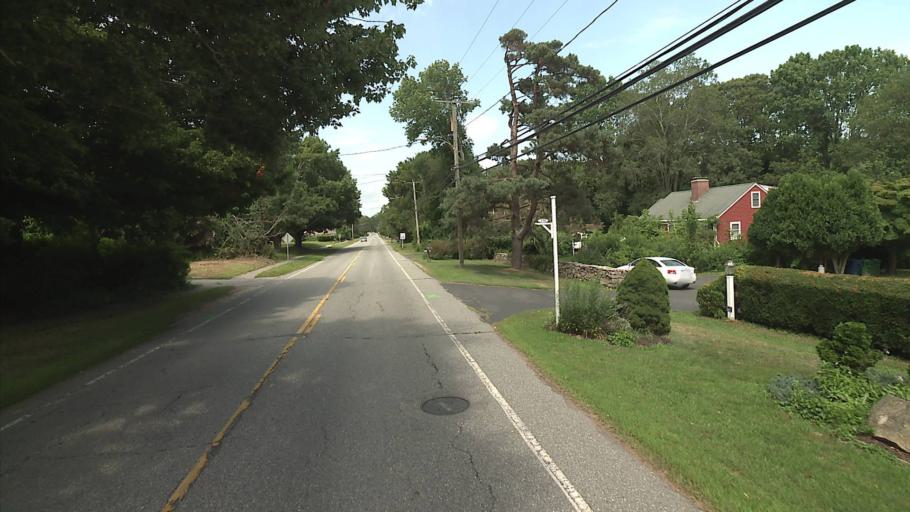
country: US
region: Connecticut
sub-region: New London County
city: Central Waterford
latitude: 41.3192
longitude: -72.1335
